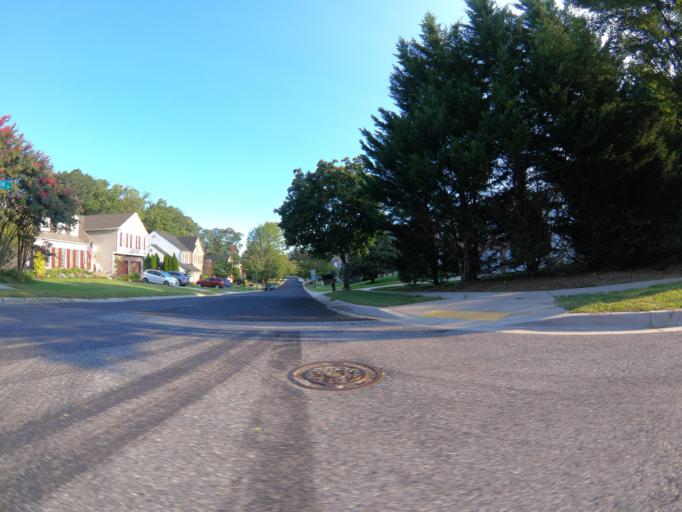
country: US
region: Maryland
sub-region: Anne Arundel County
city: South Gate
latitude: 39.1074
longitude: -76.6080
